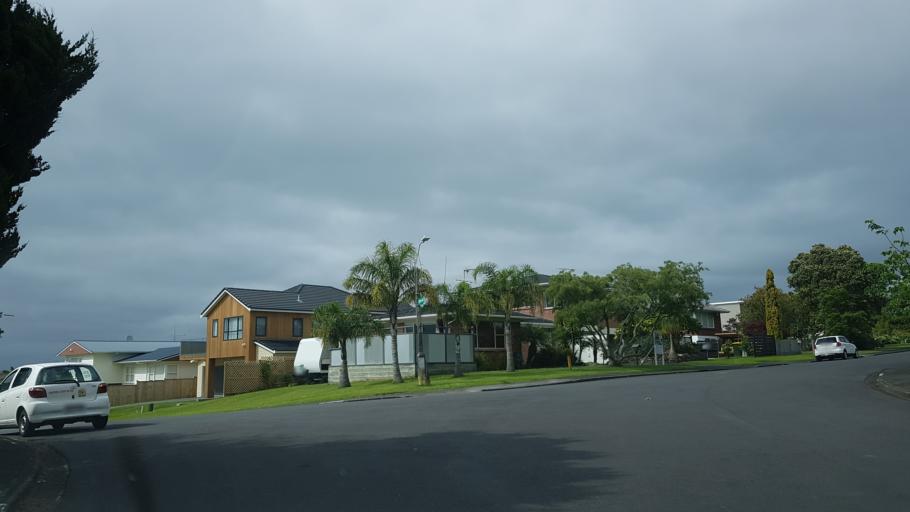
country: NZ
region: Auckland
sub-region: Auckland
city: North Shore
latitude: -36.8044
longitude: 174.7558
